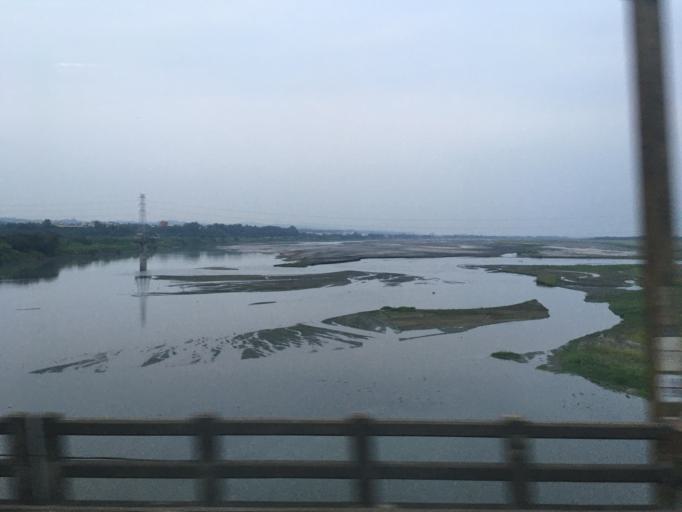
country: TW
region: Taiwan
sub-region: Pingtung
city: Pingtung
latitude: 22.6624
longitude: 120.4320
